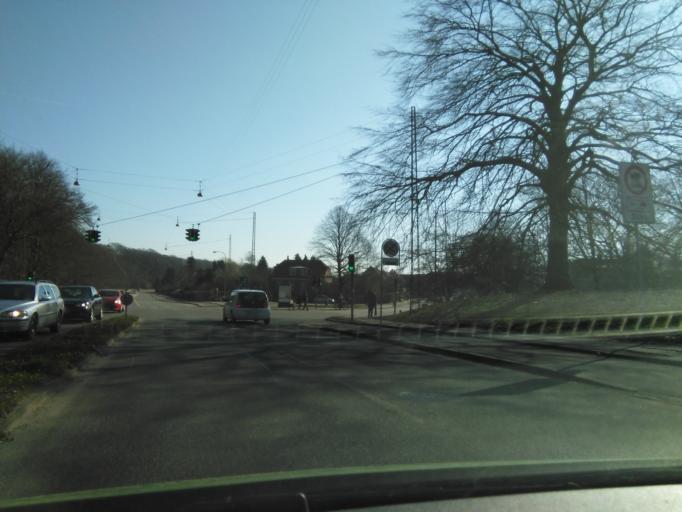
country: DK
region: Central Jutland
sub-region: Arhus Kommune
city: Arhus
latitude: 56.1778
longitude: 10.2188
